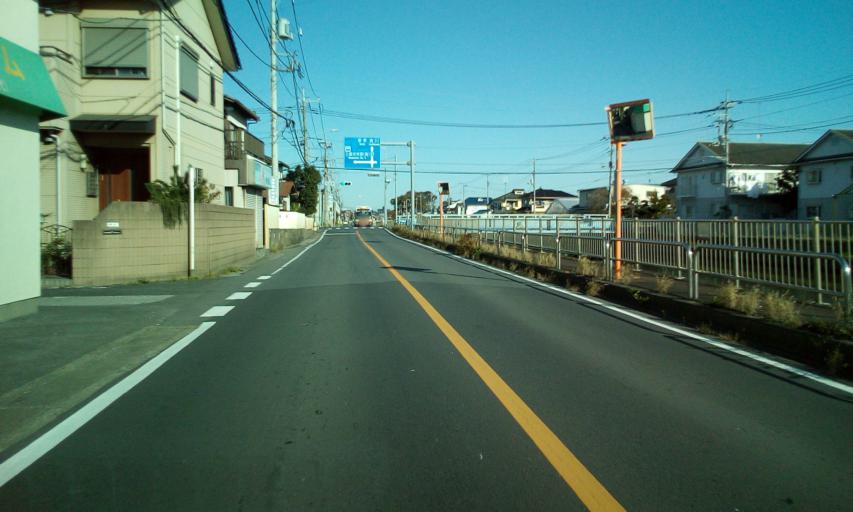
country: JP
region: Chiba
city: Nagareyama
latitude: 35.8216
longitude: 139.8832
